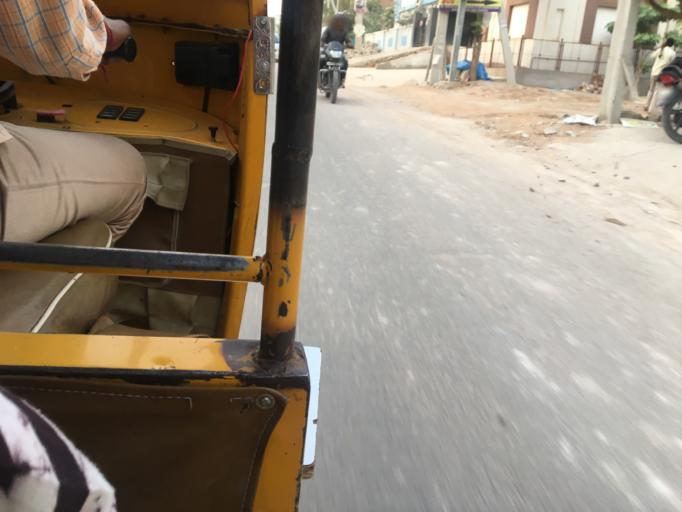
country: IN
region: Telangana
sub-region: Medak
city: Serilingampalle
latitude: 17.4304
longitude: 78.3330
